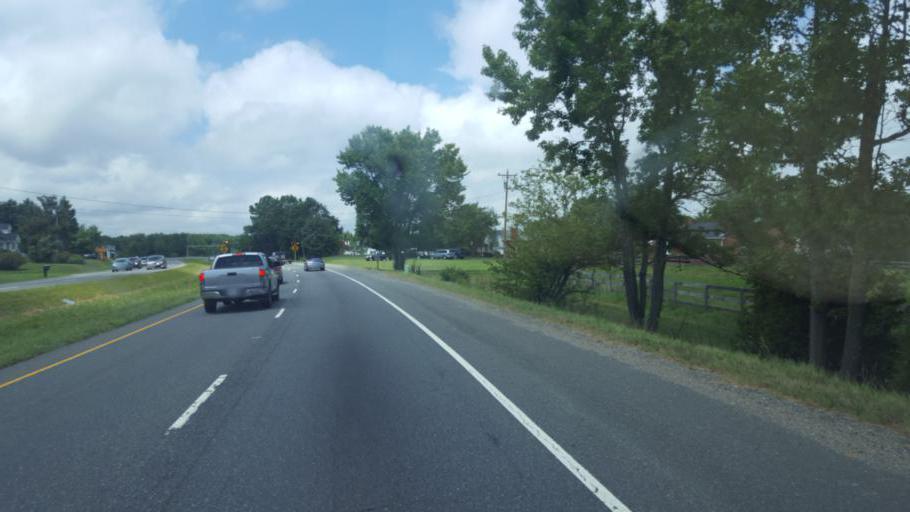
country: US
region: Virginia
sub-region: Stafford County
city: Falmouth
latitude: 38.3801
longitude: -77.5386
